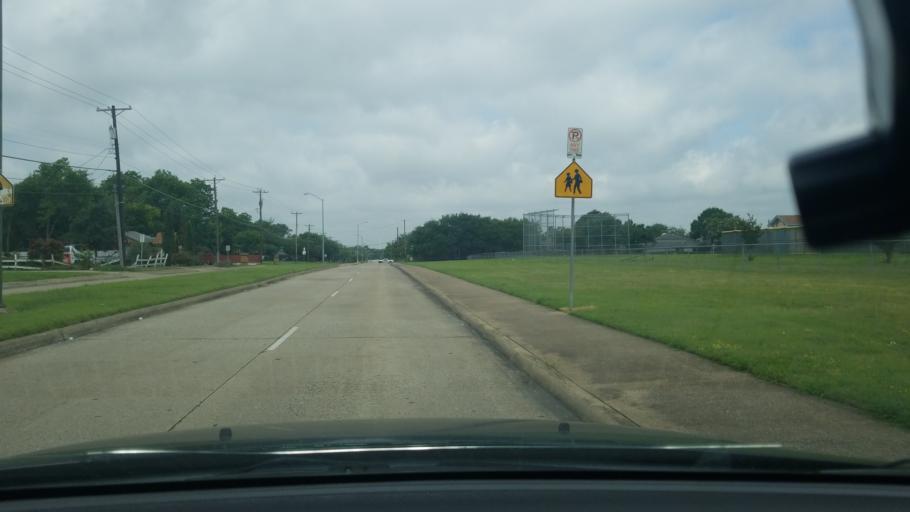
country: US
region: Texas
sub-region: Dallas County
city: Balch Springs
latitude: 32.7782
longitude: -96.6927
